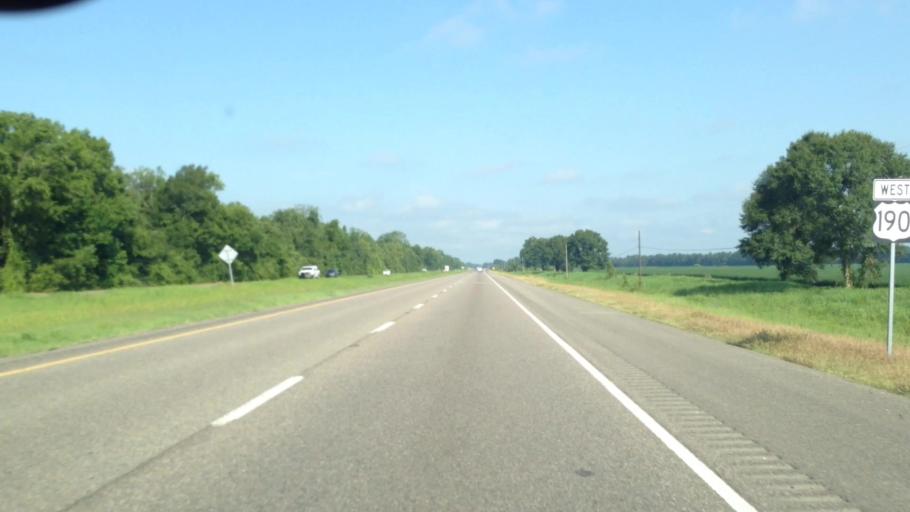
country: US
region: Louisiana
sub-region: West Baton Rouge Parish
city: Erwinville
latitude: 30.5191
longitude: -91.3653
